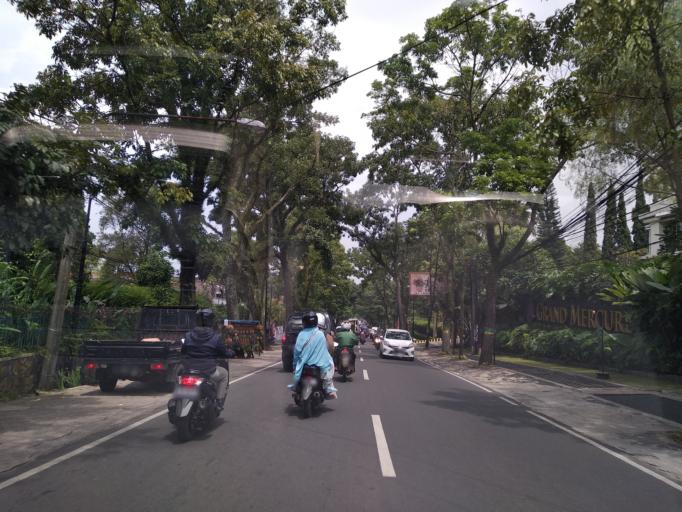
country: ID
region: West Java
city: Lembang
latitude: -6.8546
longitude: 107.5960
